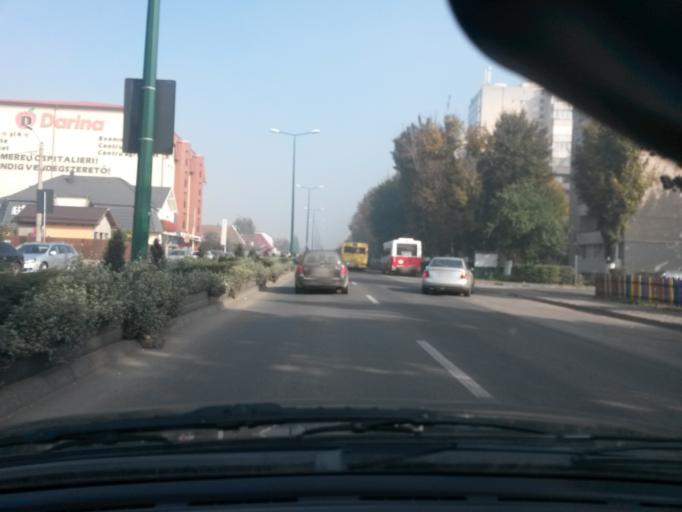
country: RO
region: Mures
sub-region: Comuna Sancraiu de Mures
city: Sancraiu de Mures
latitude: 46.5229
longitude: 24.5337
